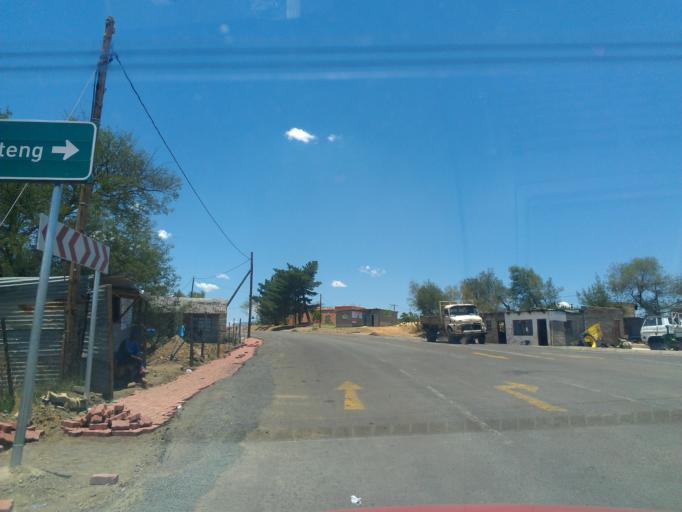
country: LS
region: Berea
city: Teyateyaneng
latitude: -29.1018
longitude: 27.9597
